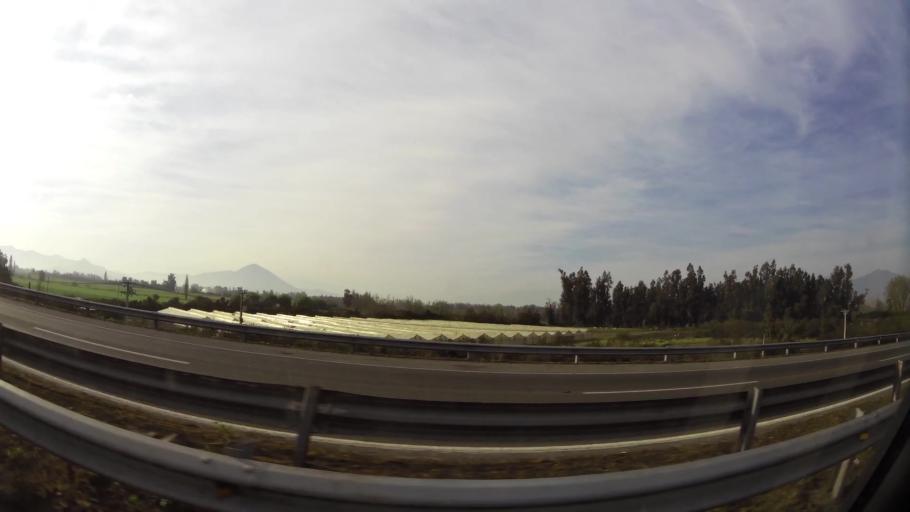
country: CL
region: Santiago Metropolitan
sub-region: Provincia de Talagante
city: Talagante
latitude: -33.6676
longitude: -70.9125
